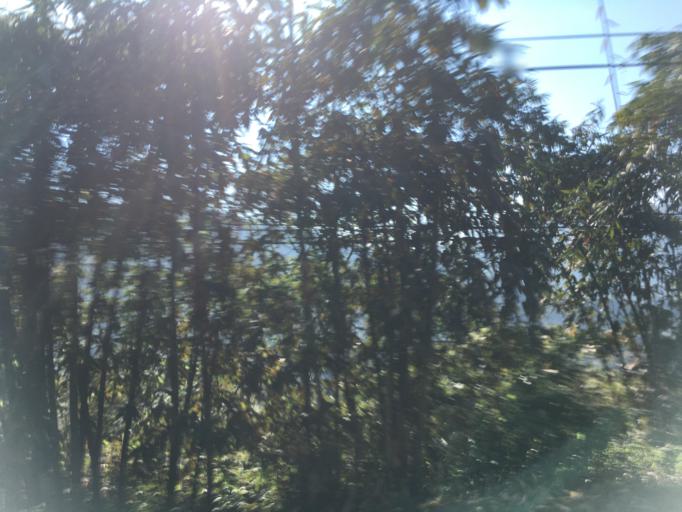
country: TW
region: Taiwan
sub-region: Chiayi
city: Jiayi Shi
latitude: 23.4109
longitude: 120.6487
